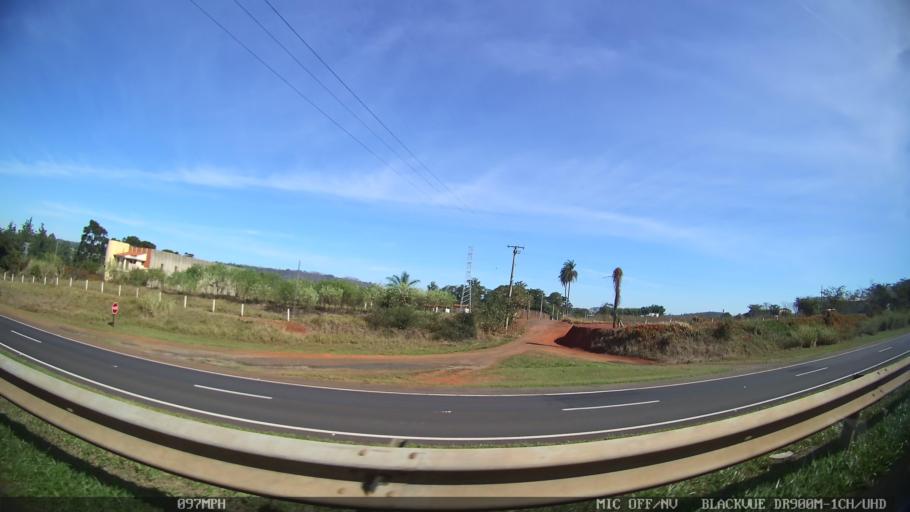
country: BR
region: Sao Paulo
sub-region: Pirassununga
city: Pirassununga
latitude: -21.9893
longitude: -47.4490
